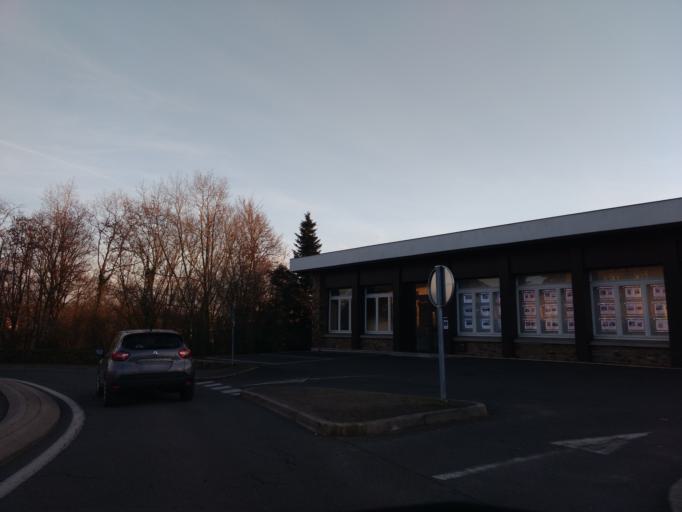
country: FR
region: Midi-Pyrenees
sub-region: Departement de l'Aveyron
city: Naucelle
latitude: 44.1960
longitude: 2.3433
